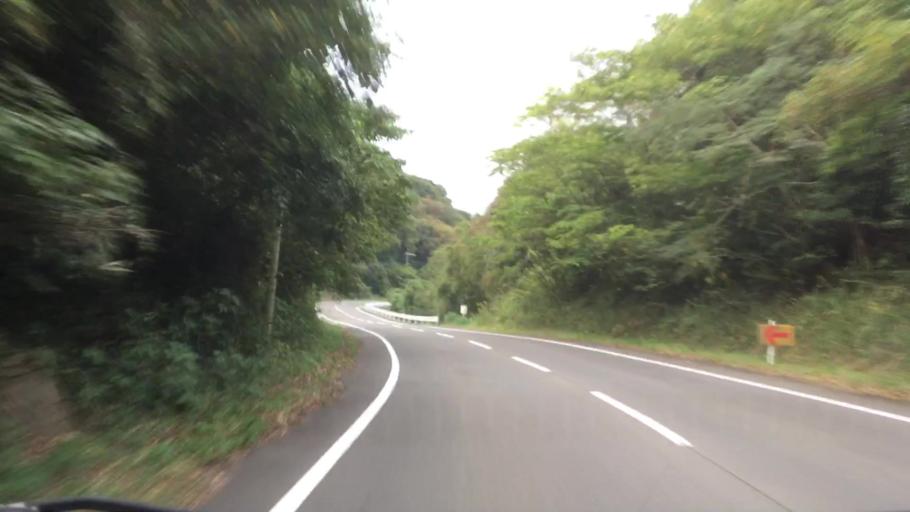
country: JP
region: Nagasaki
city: Sasebo
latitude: 32.9805
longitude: 129.7151
